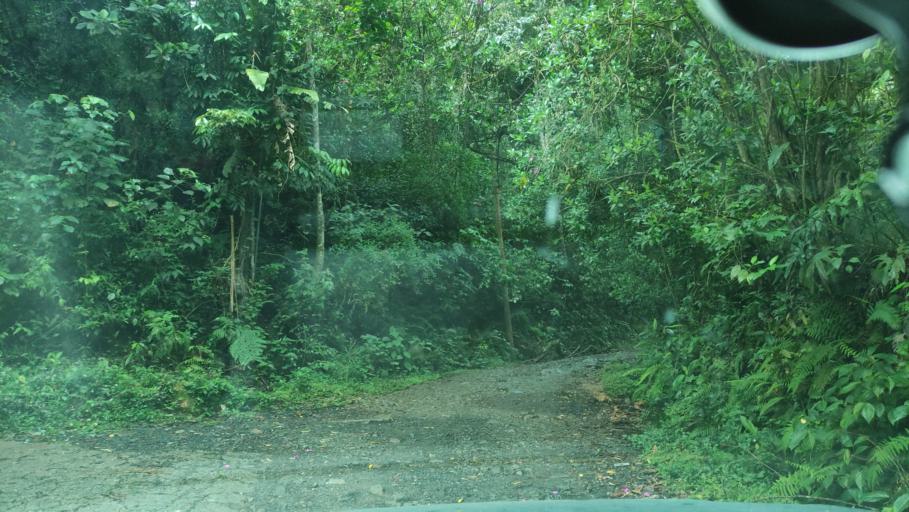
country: CO
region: Valle del Cauca
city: Jamundi
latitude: 3.3220
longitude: -76.6332
